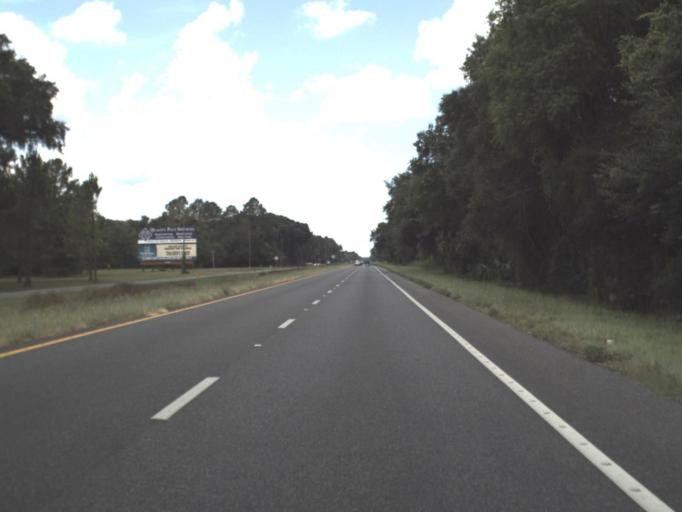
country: US
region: Florida
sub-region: Taylor County
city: Perry
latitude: 30.1489
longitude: -83.6133
